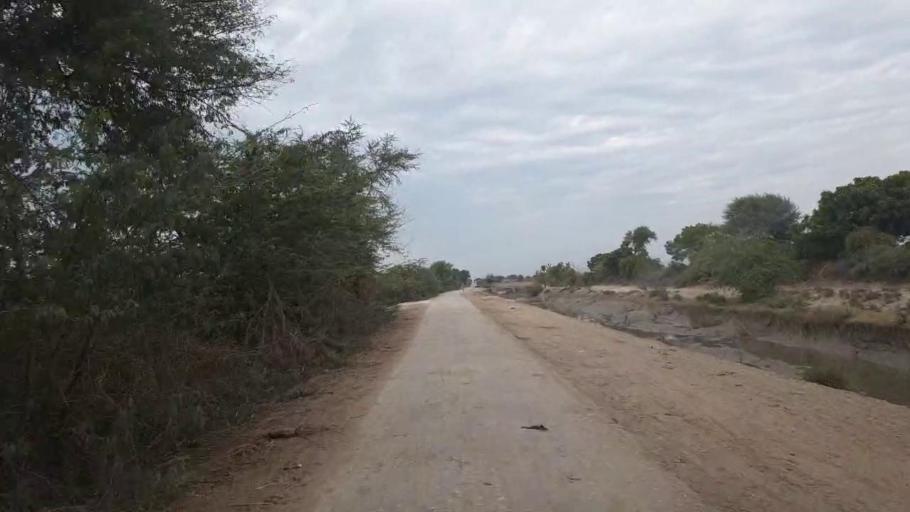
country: PK
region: Sindh
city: Jhol
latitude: 25.9871
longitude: 68.8987
